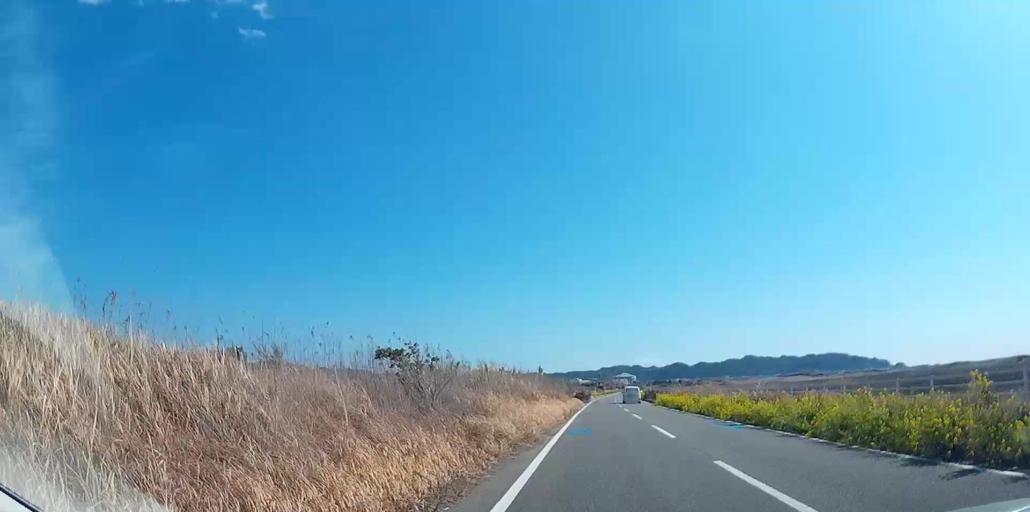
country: JP
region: Chiba
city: Tateyama
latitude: 34.9443
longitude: 139.8162
